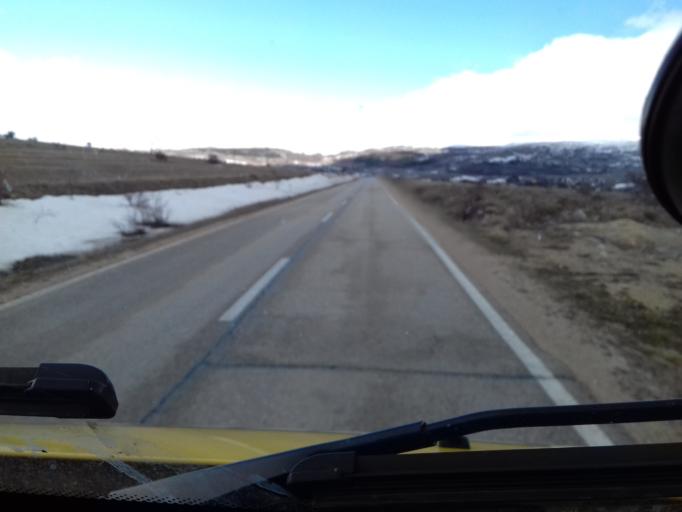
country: BA
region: Federation of Bosnia and Herzegovina
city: Tomislavgrad
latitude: 43.7435
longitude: 17.2260
